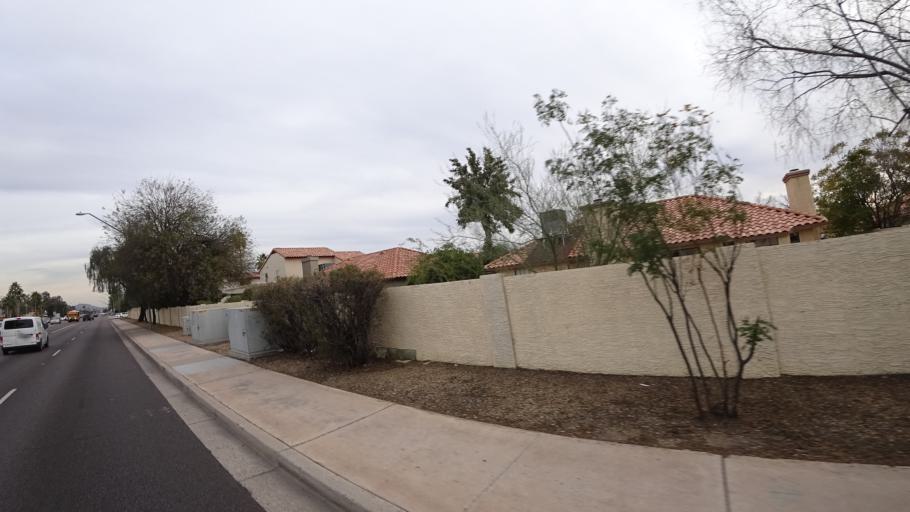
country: US
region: Arizona
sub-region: Maricopa County
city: Glendale
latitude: 33.5818
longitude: -112.1745
